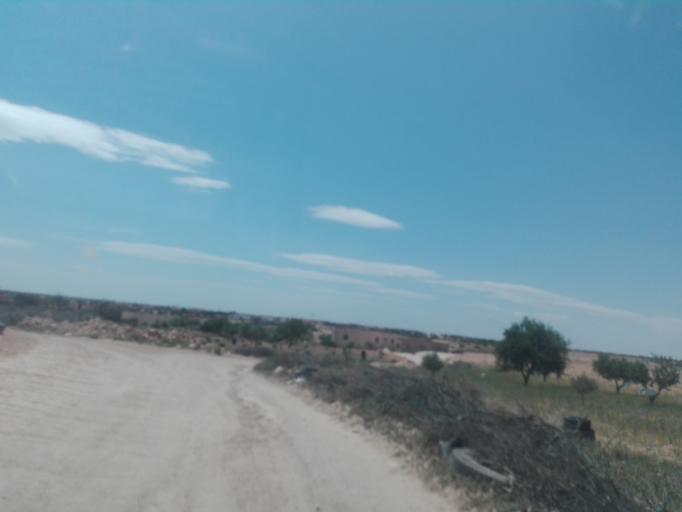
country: TN
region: Safaqis
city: Sfax
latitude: 34.6660
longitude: 10.5683
